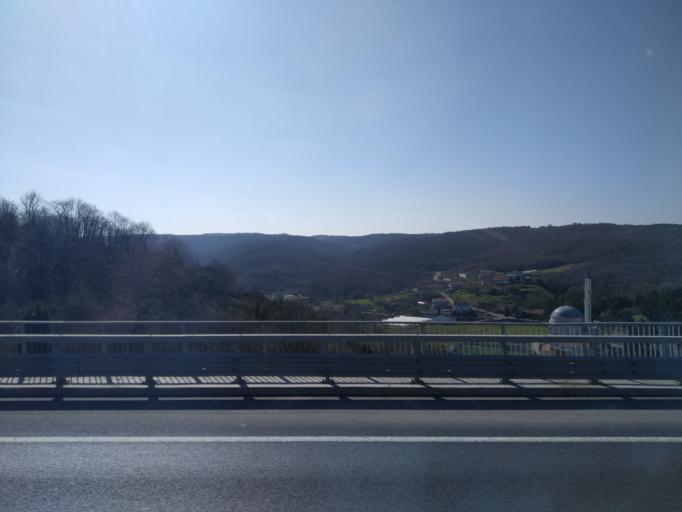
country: TR
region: Istanbul
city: Mahmut Sevket Pasa
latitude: 41.1803
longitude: 29.2353
